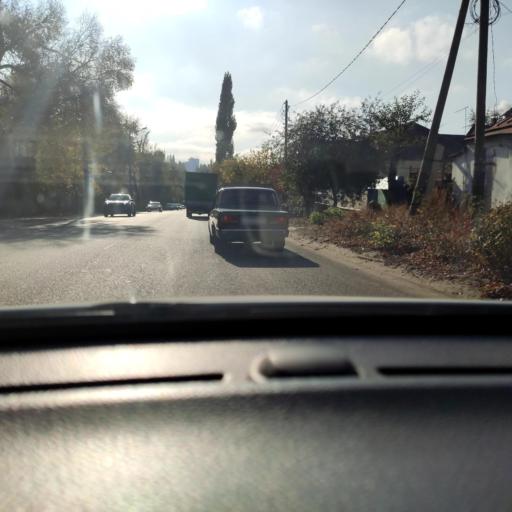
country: RU
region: Voronezj
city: Voronezh
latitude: 51.6961
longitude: 39.1643
